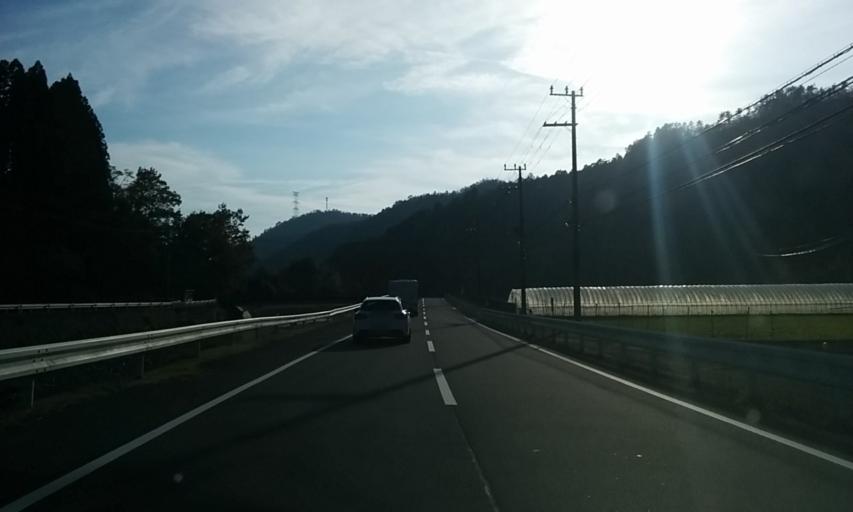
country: JP
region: Kyoto
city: Kameoka
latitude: 35.1863
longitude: 135.5166
